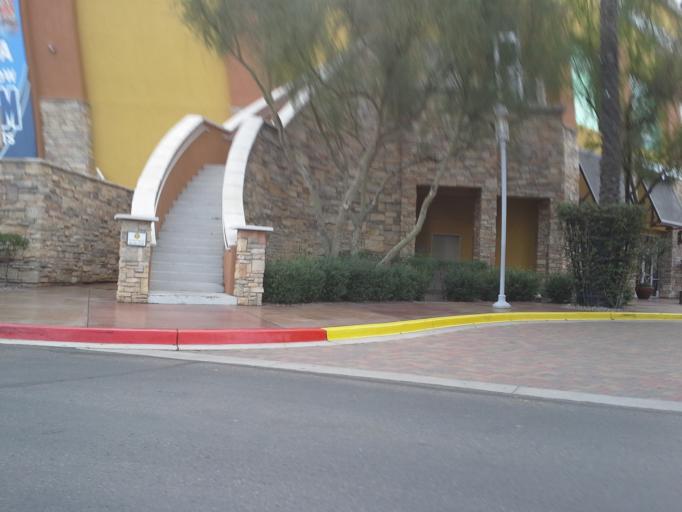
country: US
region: Arizona
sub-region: Maricopa County
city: Paradise Valley
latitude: 33.6773
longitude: -111.9733
